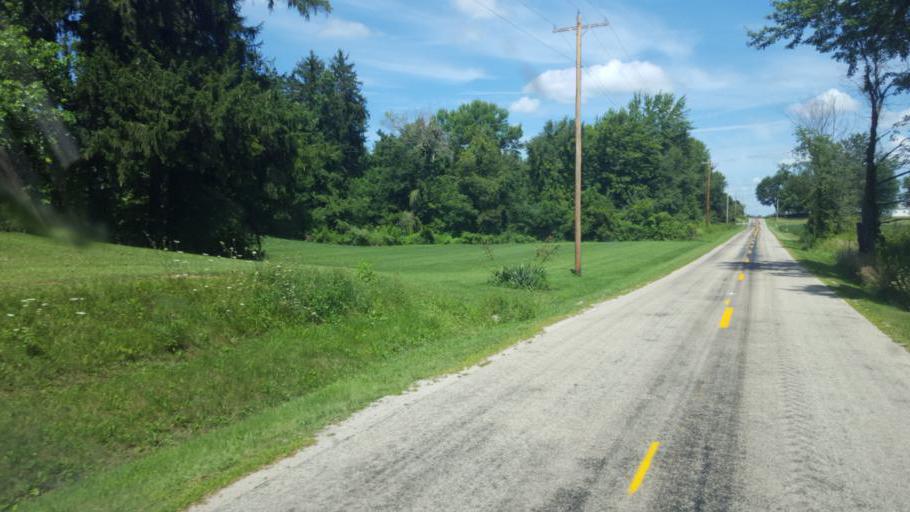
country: US
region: Ohio
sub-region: Delaware County
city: Sunbury
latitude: 40.3069
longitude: -82.8079
